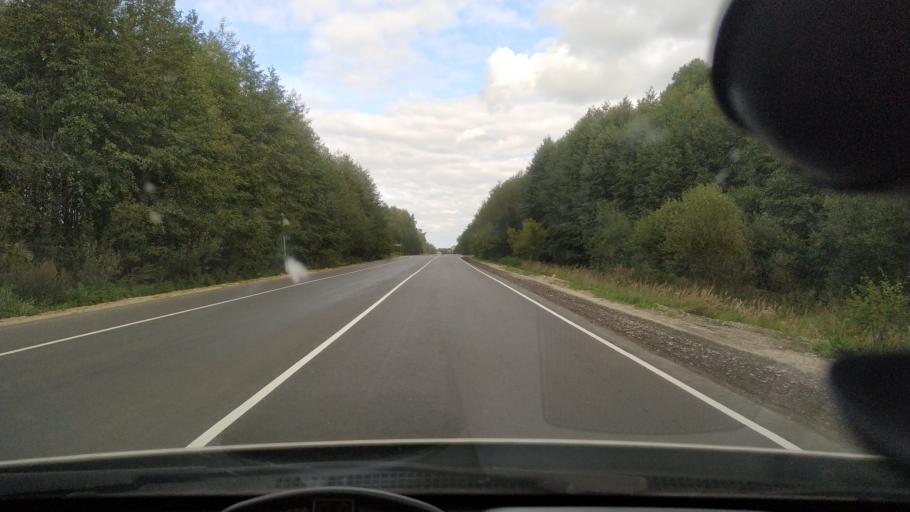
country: RU
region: Moskovskaya
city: Kabanovo
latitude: 55.7363
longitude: 38.9222
